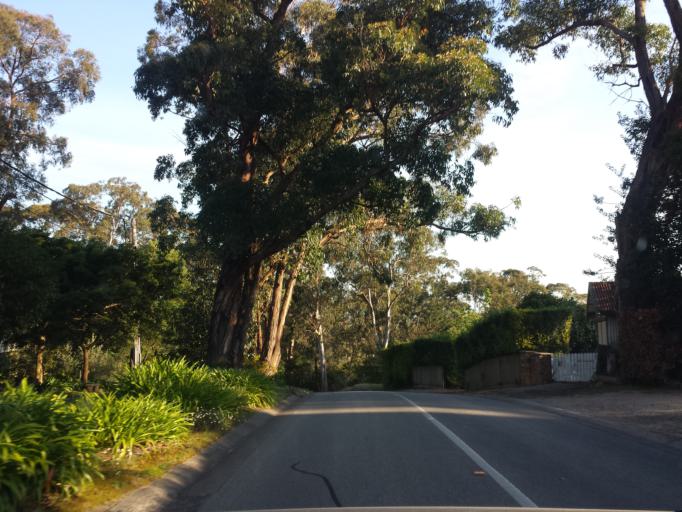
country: AU
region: Victoria
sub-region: Yarra Ranges
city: Belgrave
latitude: -37.9040
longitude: 145.3521
